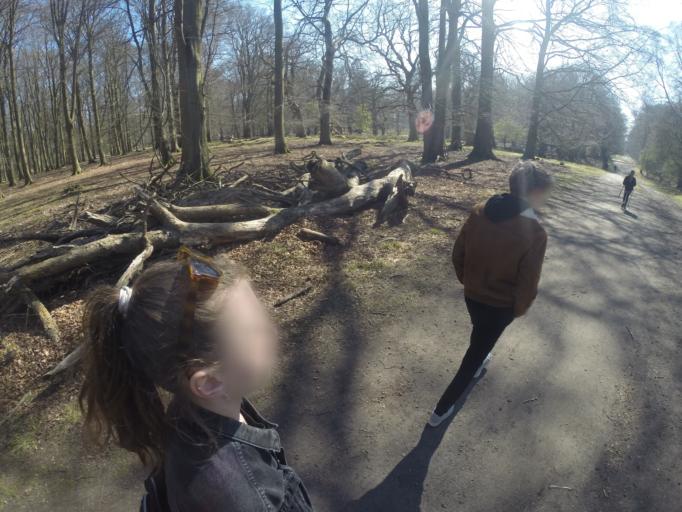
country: DK
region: Capital Region
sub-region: Gentofte Kommune
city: Charlottenlund
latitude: 55.7813
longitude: 12.5526
